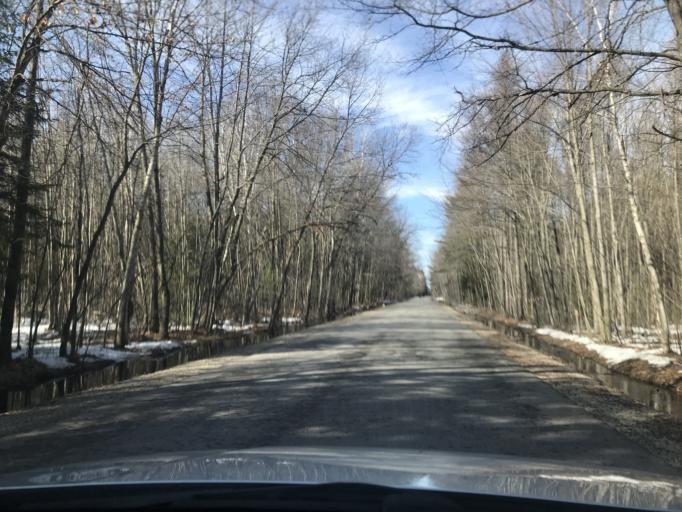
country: US
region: Wisconsin
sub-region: Marinette County
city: Marinette
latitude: 45.0237
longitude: -87.6674
